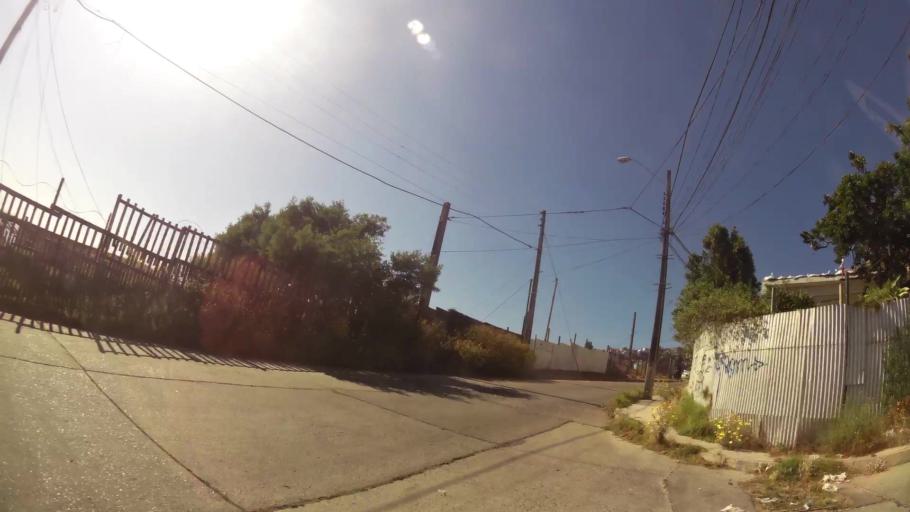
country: CL
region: Valparaiso
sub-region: Provincia de Valparaiso
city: Valparaiso
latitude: -33.0495
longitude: -71.6374
